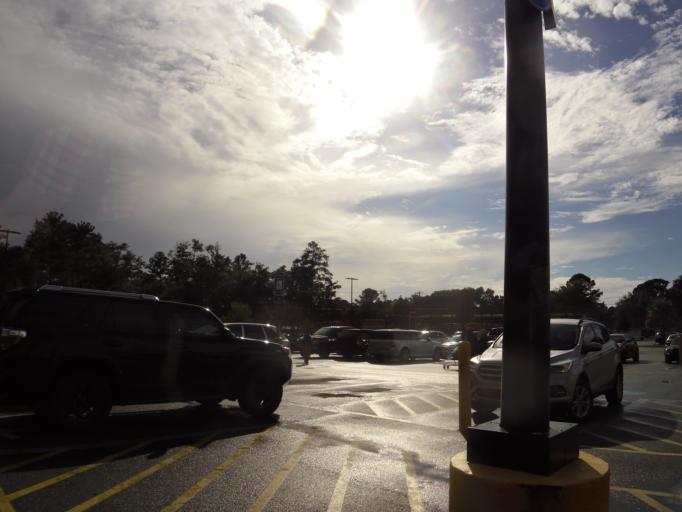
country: US
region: Georgia
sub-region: Liberty County
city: Walthourville
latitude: 31.7964
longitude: -81.6054
